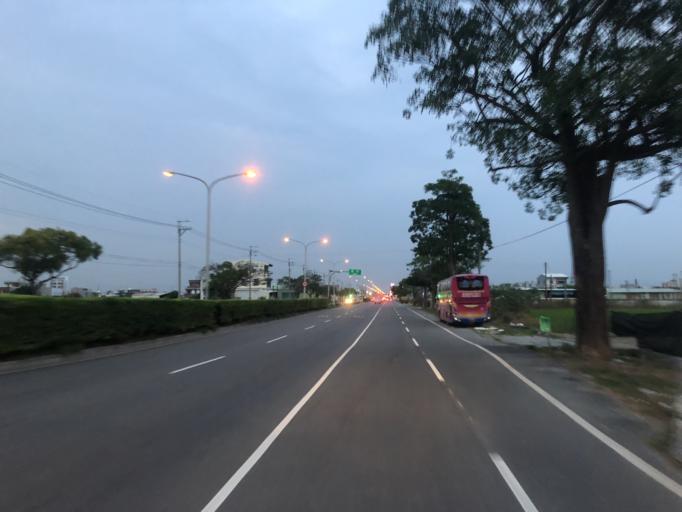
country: TW
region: Taiwan
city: Yujing
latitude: 23.1318
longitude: 120.3206
